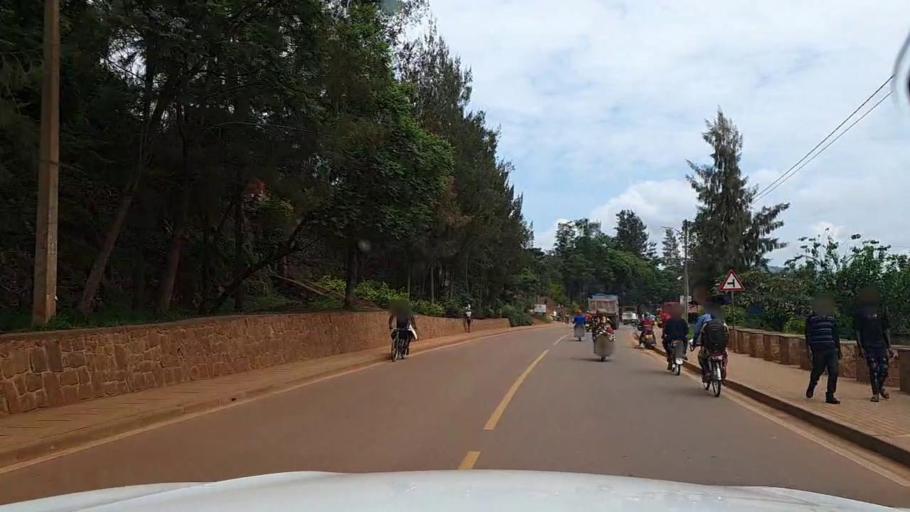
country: RW
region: Kigali
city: Kigali
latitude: -1.9254
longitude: 30.0463
